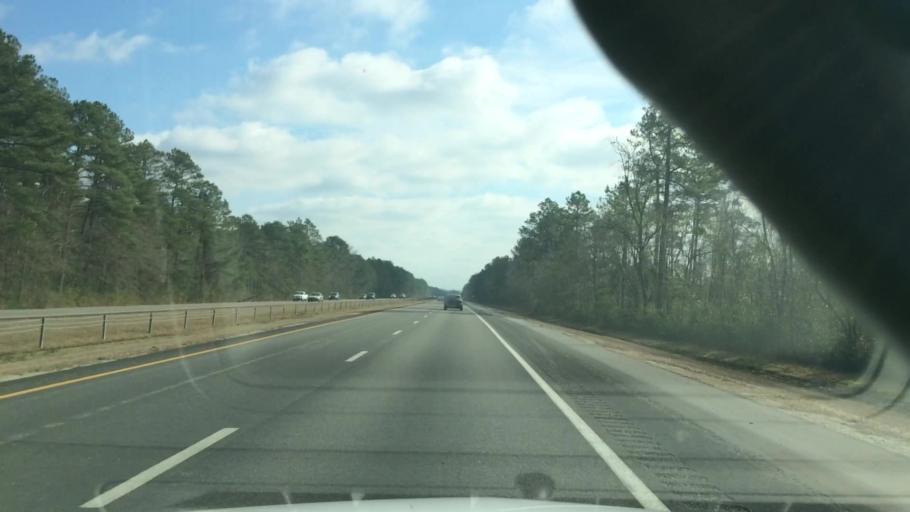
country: US
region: North Carolina
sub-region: Pender County
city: Burgaw
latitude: 34.6221
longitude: -77.9309
